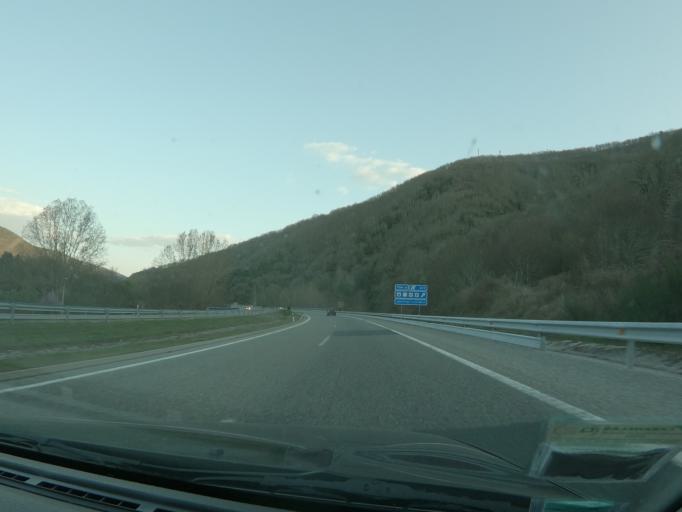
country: ES
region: Castille and Leon
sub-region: Provincia de Leon
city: Trabadelo
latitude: 42.6501
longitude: -6.8896
